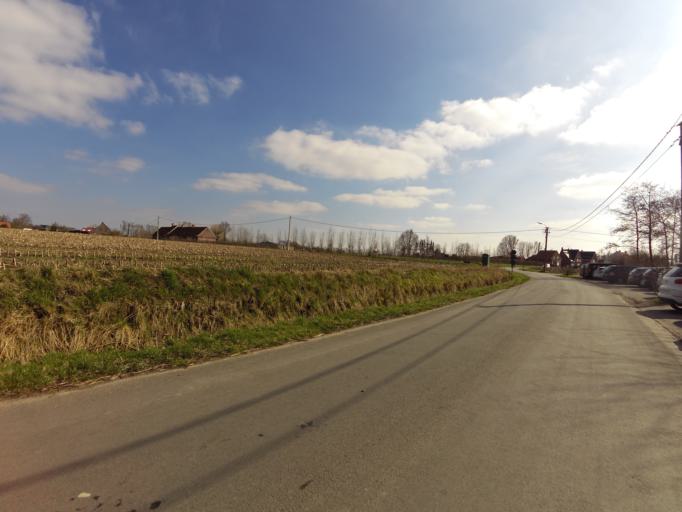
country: BE
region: Flanders
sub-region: Provincie West-Vlaanderen
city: Torhout
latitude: 51.0535
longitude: 3.0960
